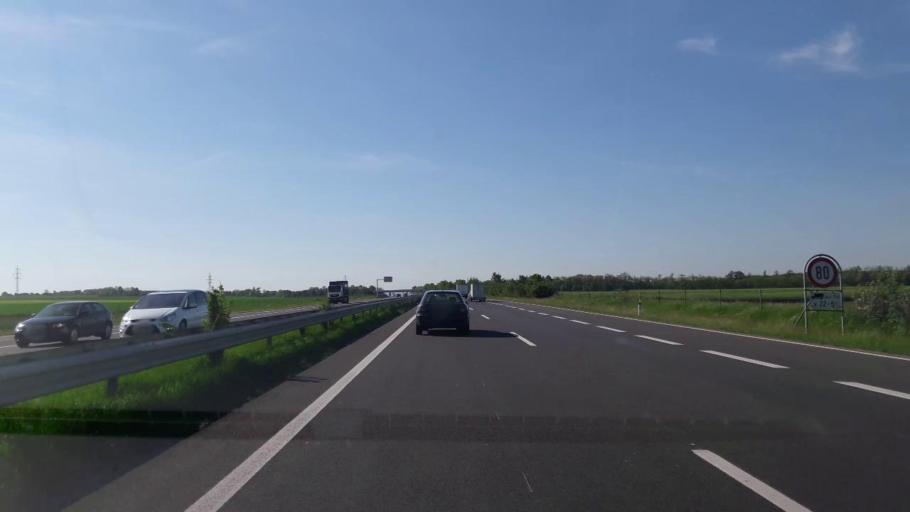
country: AT
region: Burgenland
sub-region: Eisenstadt-Umgebung
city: Hornstein
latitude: 47.8651
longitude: 16.4210
